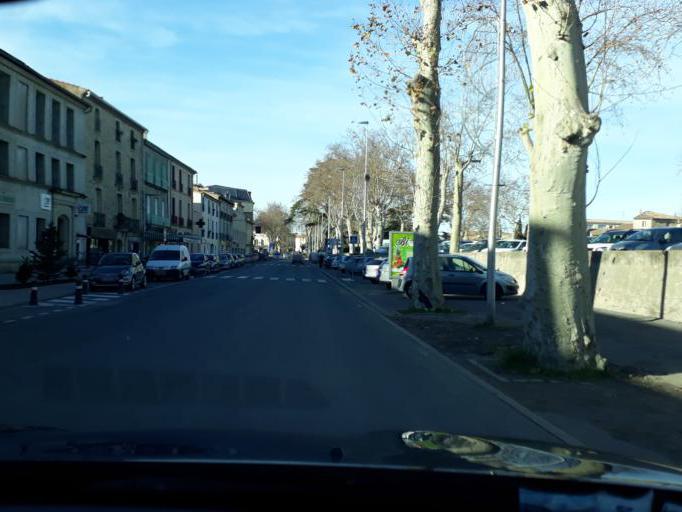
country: FR
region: Languedoc-Roussillon
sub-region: Departement de l'Herault
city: Pezenas
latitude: 43.4598
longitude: 3.4272
